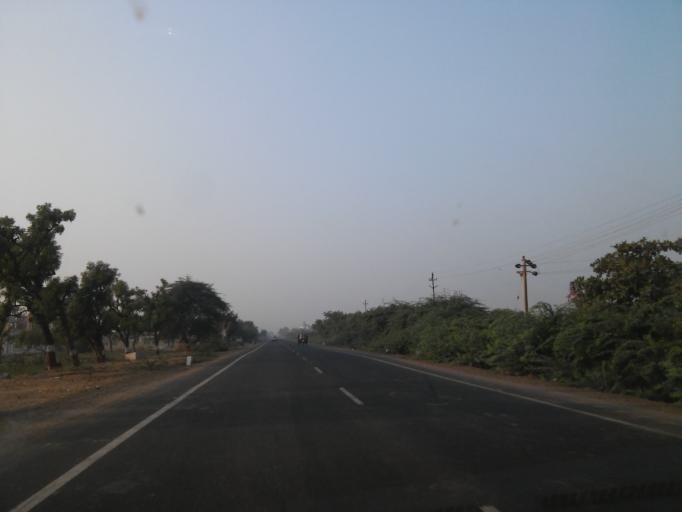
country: IN
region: Gujarat
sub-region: Kachchh
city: Mandvi
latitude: 22.8559
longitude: 69.3827
